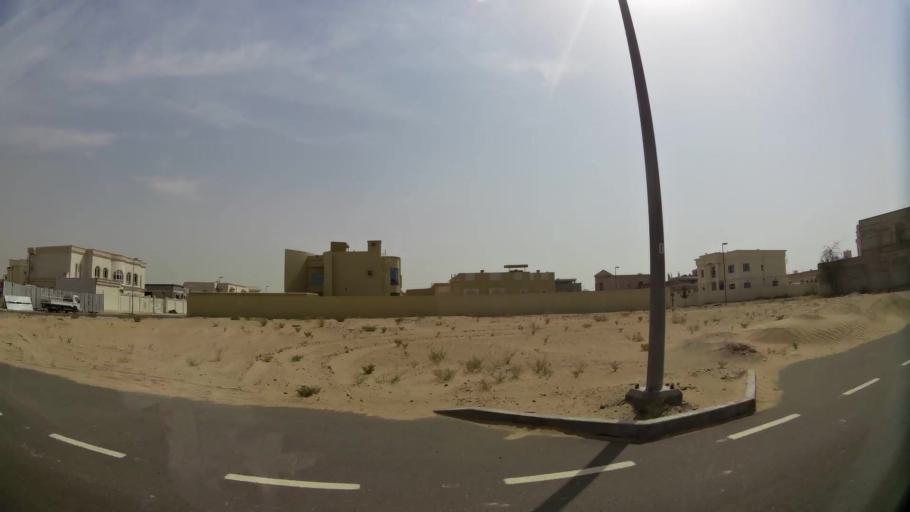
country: AE
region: Ash Shariqah
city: Sharjah
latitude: 25.2615
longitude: 55.4665
